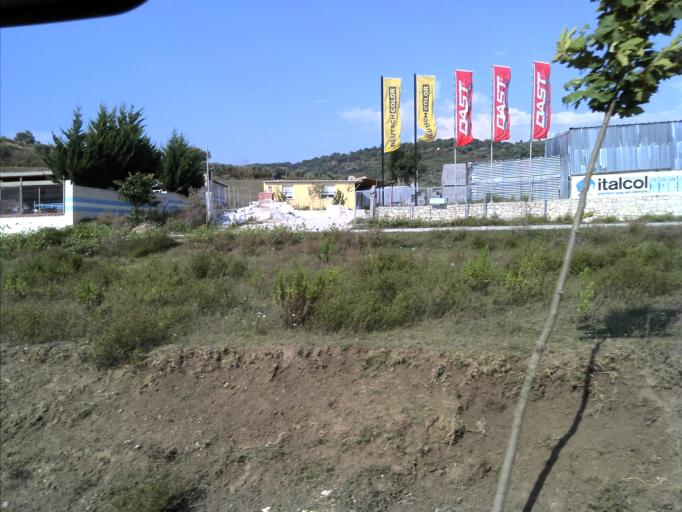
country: AL
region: Fier
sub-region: Rrethi i Mallakastres
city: Fratar
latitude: 40.4990
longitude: 19.8210
